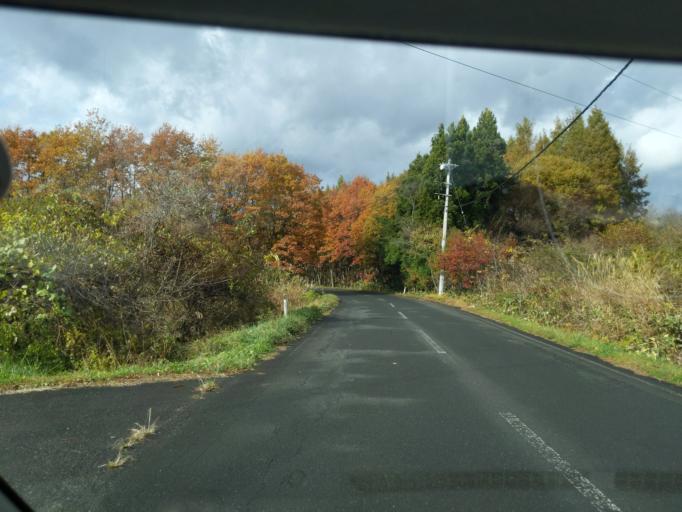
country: JP
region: Iwate
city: Mizusawa
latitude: 39.0961
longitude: 141.0080
